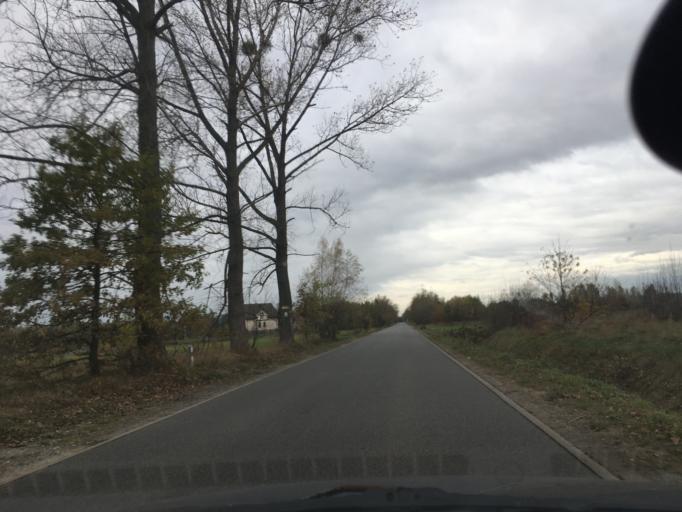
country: PL
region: Lodz Voivodeship
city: Zabia Wola
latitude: 52.0213
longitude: 20.7188
